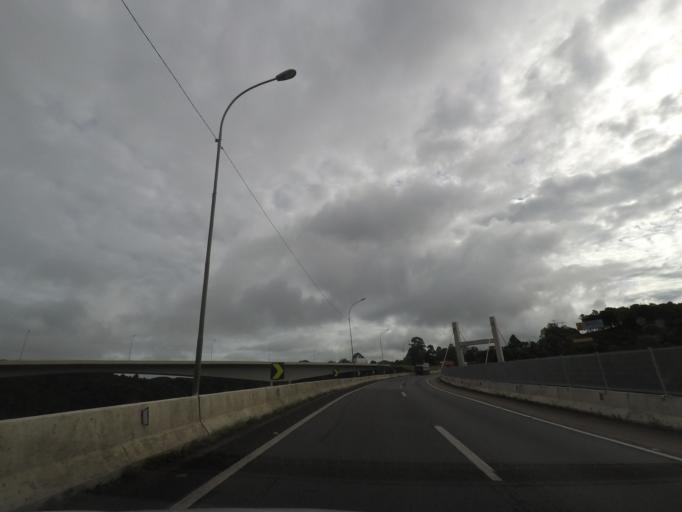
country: BR
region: Parana
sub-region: Campina Grande Do Sul
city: Campina Grande do Sul
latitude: -25.1802
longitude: -48.8796
